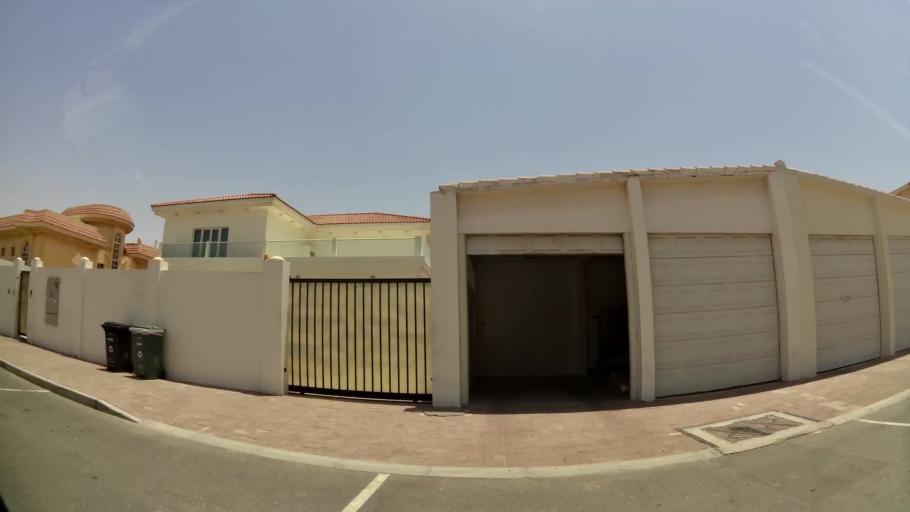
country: AE
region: Dubai
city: Dubai
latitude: 25.2043
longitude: 55.2470
